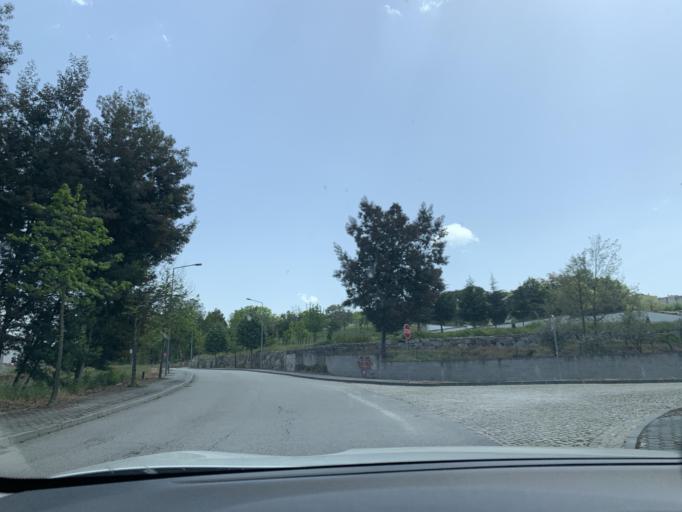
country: PT
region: Viseu
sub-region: Mangualde
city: Mangualde
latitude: 40.6091
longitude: -7.7705
